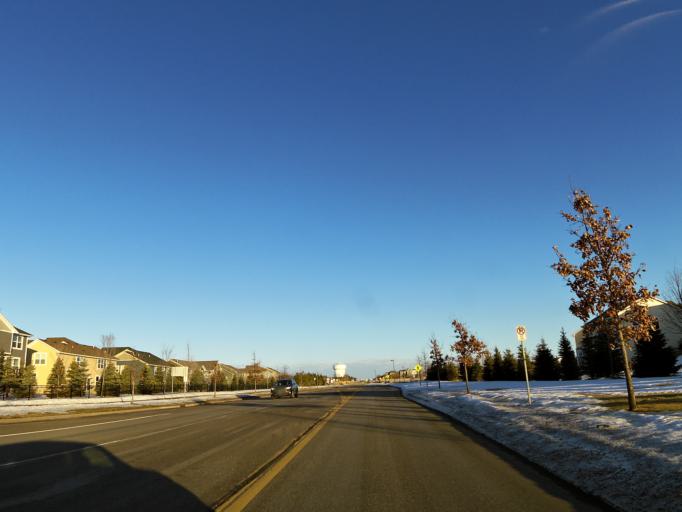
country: US
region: Minnesota
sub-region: Washington County
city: Woodbury
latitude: 44.9018
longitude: -92.8797
